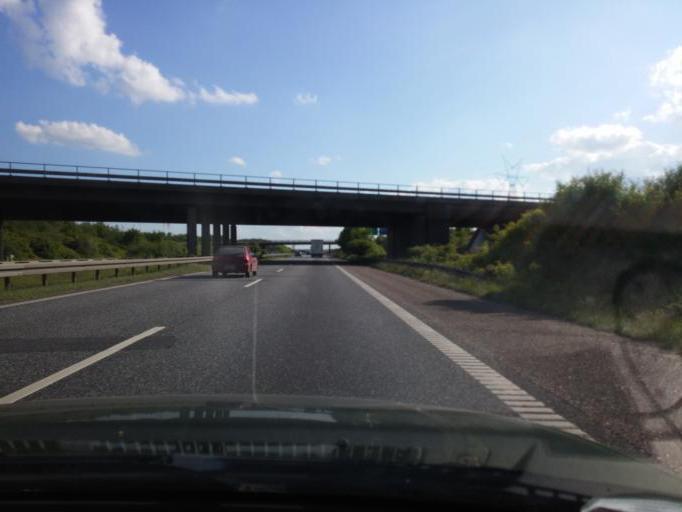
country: DK
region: South Denmark
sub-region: Kolding Kommune
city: Kolding
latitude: 55.5149
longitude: 9.4356
